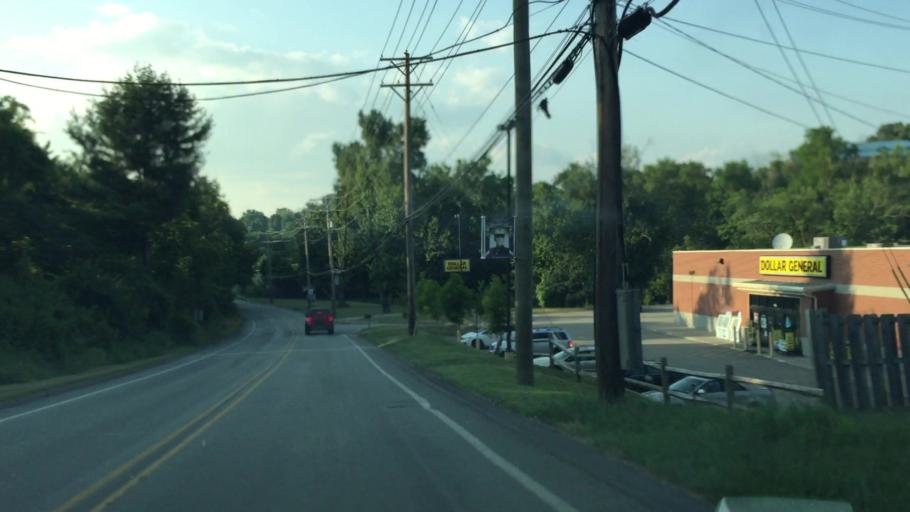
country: US
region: Pennsylvania
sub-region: Allegheny County
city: South Park Township
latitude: 40.2977
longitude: -79.9944
